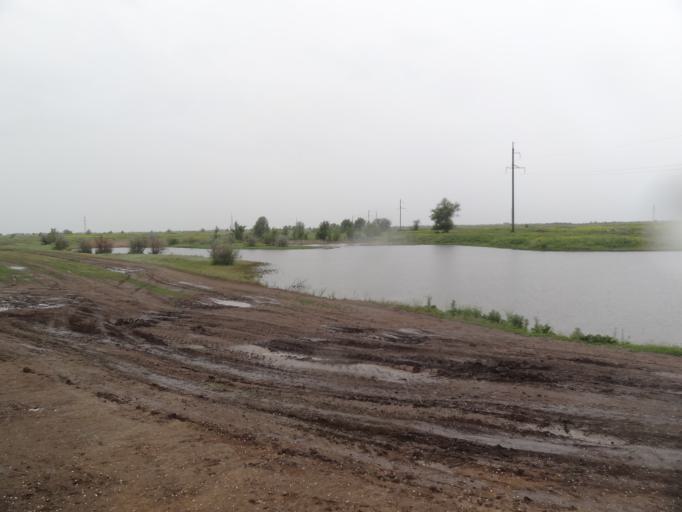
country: RU
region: Saratov
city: Engel's
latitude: 51.3704
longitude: 46.2461
